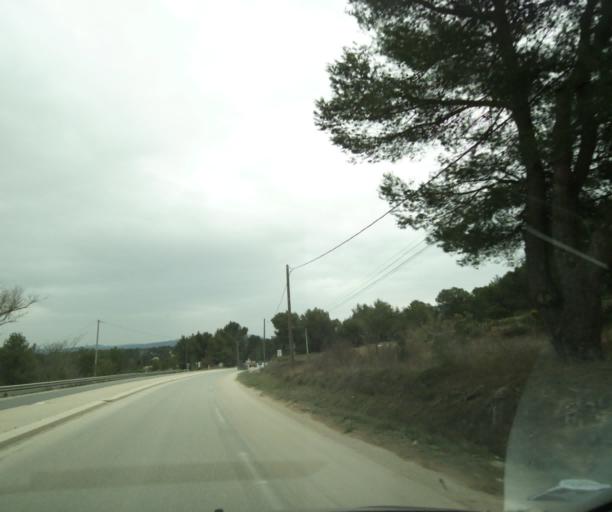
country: FR
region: Provence-Alpes-Cote d'Azur
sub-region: Departement des Bouches-du-Rhone
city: Meyrargues
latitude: 43.6312
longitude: 5.5134
